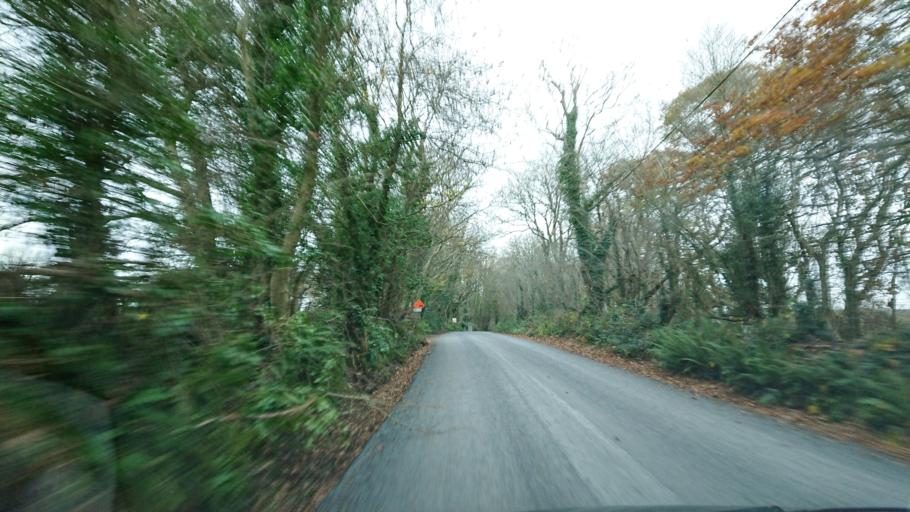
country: IE
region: Munster
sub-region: Waterford
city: Dunmore East
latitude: 52.1997
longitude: -7.0279
